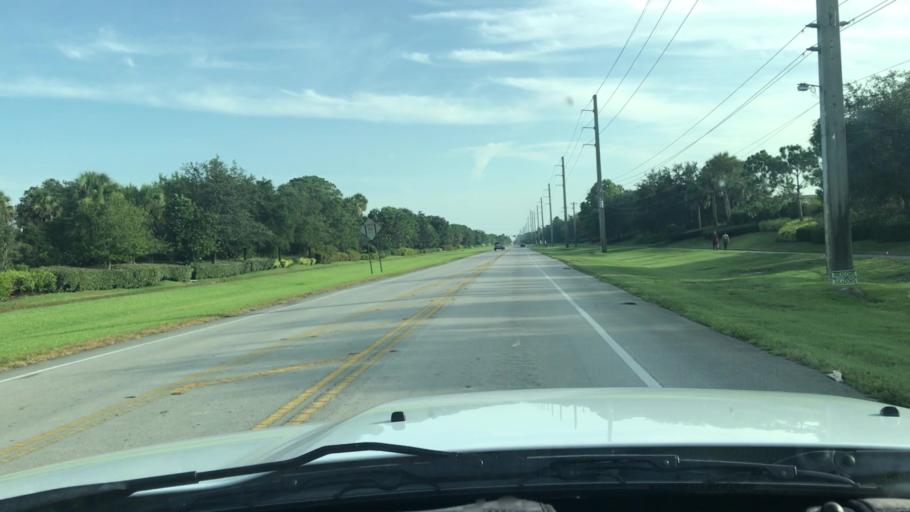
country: US
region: Florida
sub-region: Saint Lucie County
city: Lakewood Park
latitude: 27.5668
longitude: -80.4144
